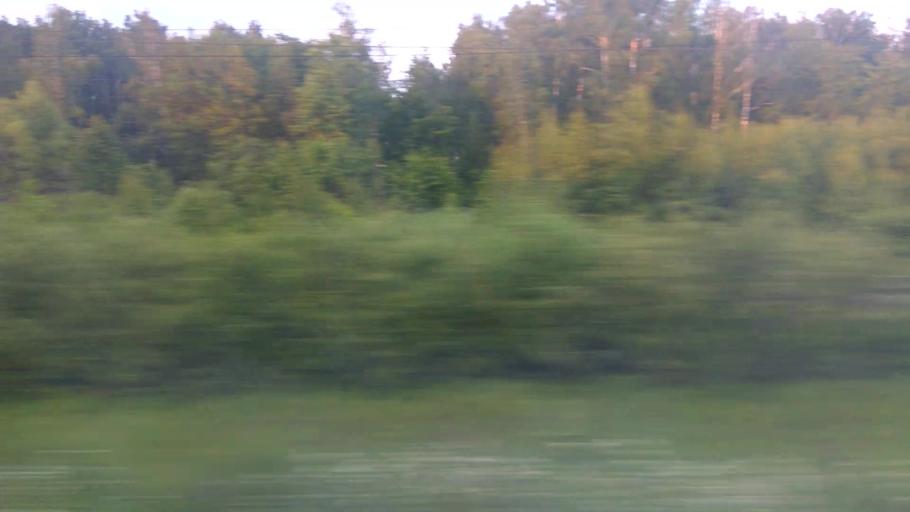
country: RU
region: Moskovskaya
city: Il'inskoye
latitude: 55.2013
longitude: 37.9226
